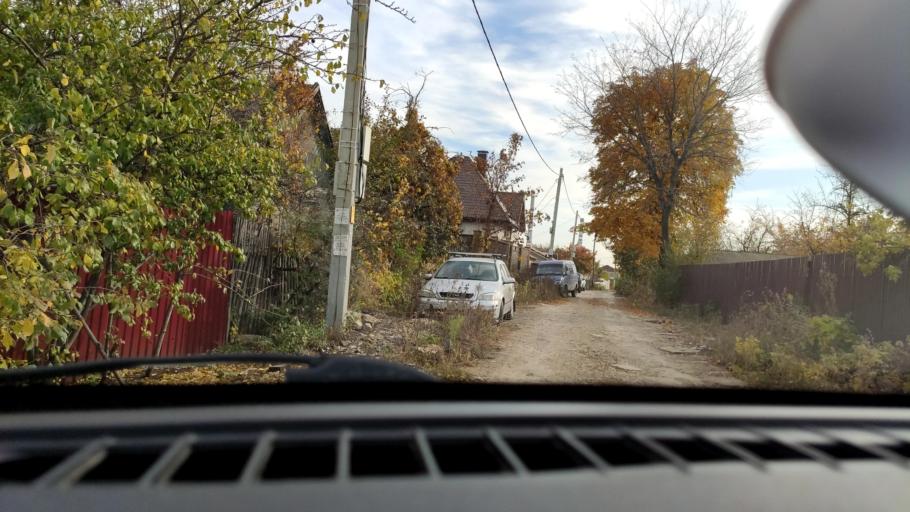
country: RU
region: Samara
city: Petra-Dubrava
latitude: 53.2656
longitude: 50.2650
